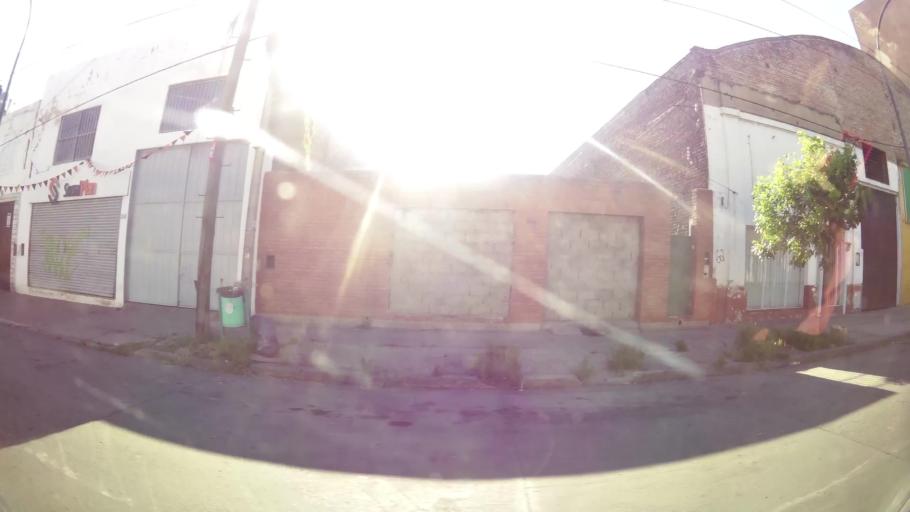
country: AR
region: Cordoba
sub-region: Departamento de Capital
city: Cordoba
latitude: -31.3942
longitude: -64.1760
